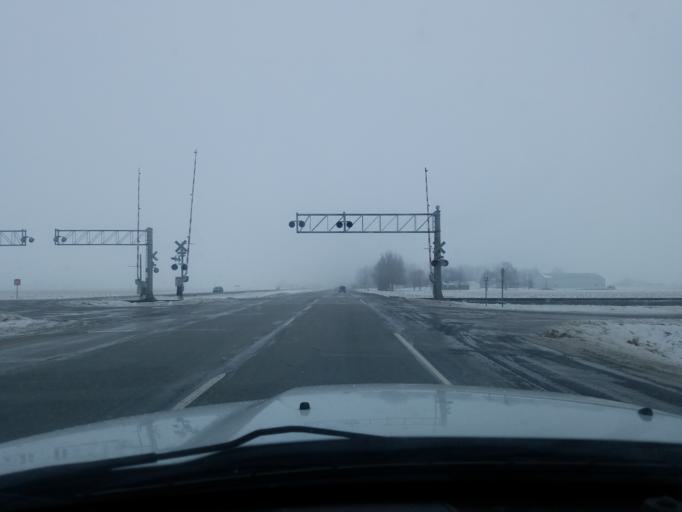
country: US
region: Indiana
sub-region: Tipton County
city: Tipton
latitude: 40.2890
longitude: -86.1268
